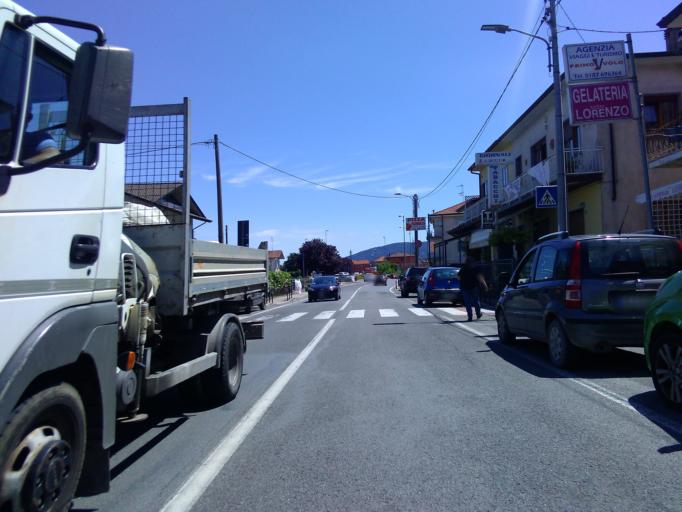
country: IT
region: Liguria
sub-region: Provincia di La Spezia
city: Santo Stefano di Magra
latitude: 44.1458
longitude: 9.9240
